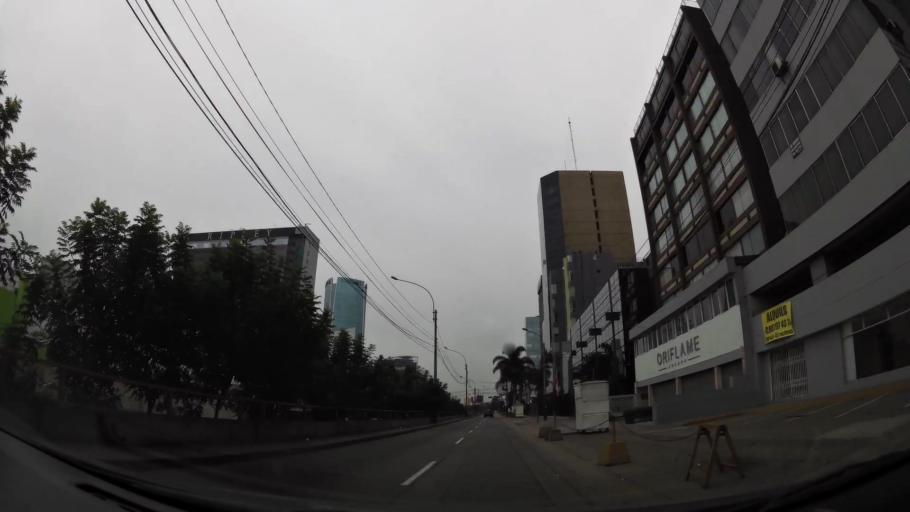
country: PE
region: Lima
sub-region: Lima
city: San Isidro
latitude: -12.0959
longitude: -77.0243
